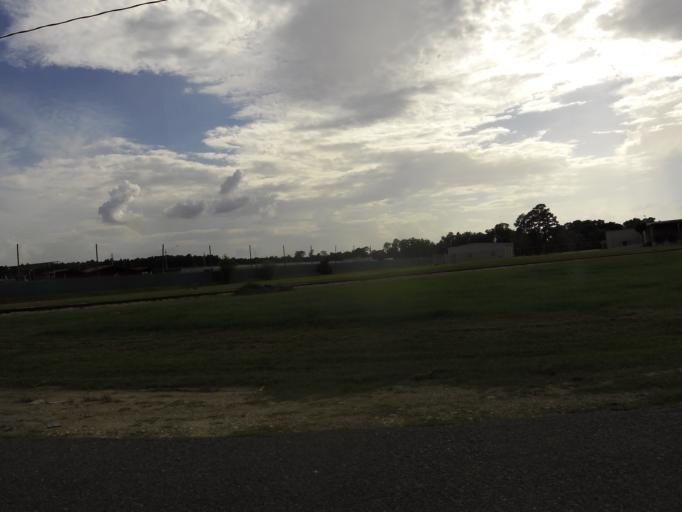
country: US
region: Florida
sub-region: Duval County
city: Jacksonville
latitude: 30.3636
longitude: -81.7111
